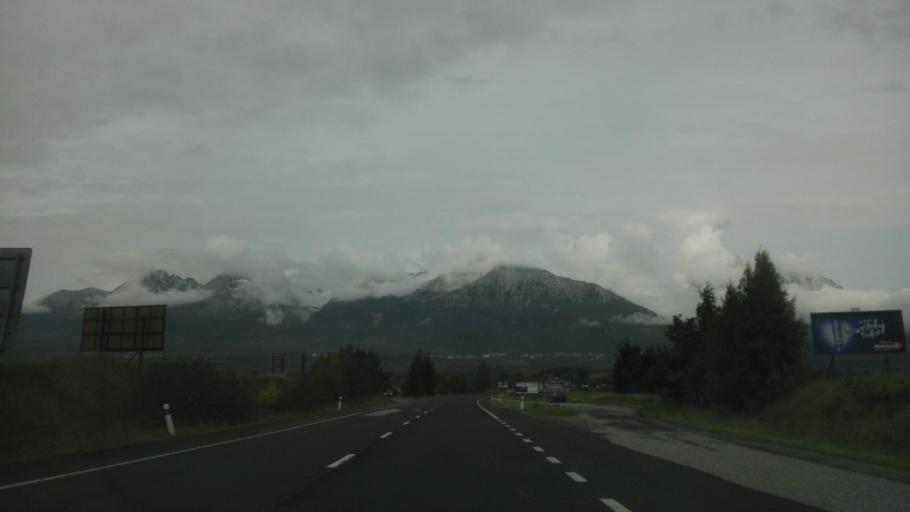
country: SK
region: Presovsky
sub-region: Okres Poprad
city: Poprad
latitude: 49.0838
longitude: 20.2667
